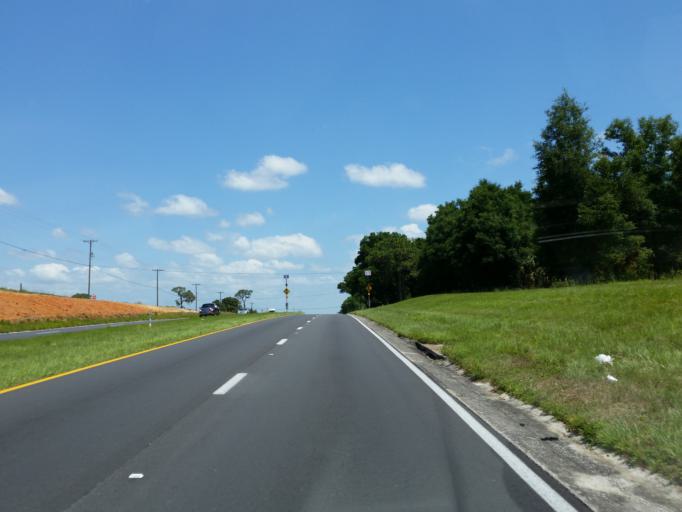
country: US
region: Florida
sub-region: Pasco County
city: Zephyrhills North
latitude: 28.2962
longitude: -82.1877
